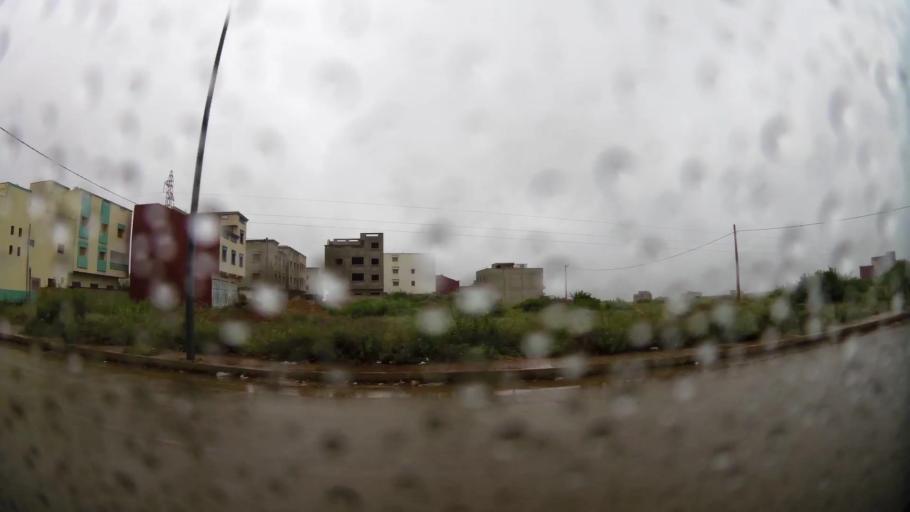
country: MA
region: Oriental
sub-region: Nador
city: Boudinar
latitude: 35.1160
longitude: -3.6439
